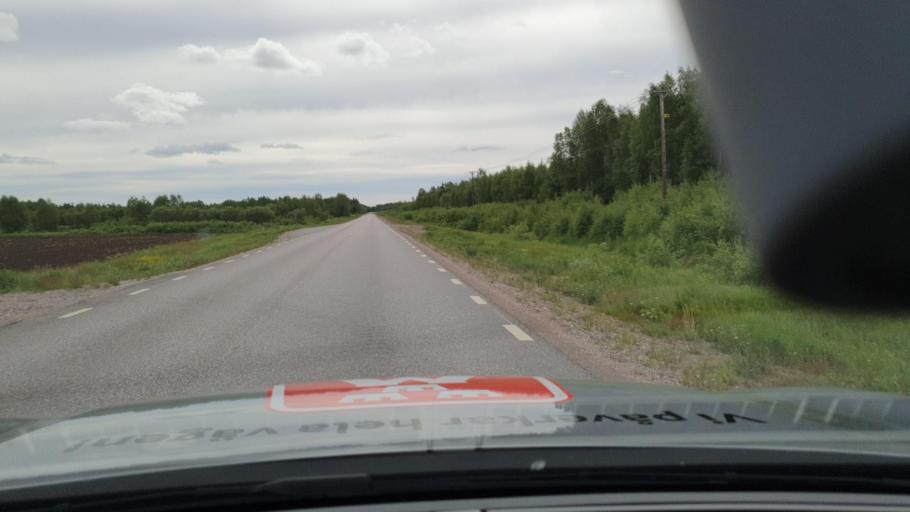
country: SE
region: Norrbotten
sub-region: Kalix Kommun
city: Kalix
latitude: 65.8885
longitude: 23.4710
